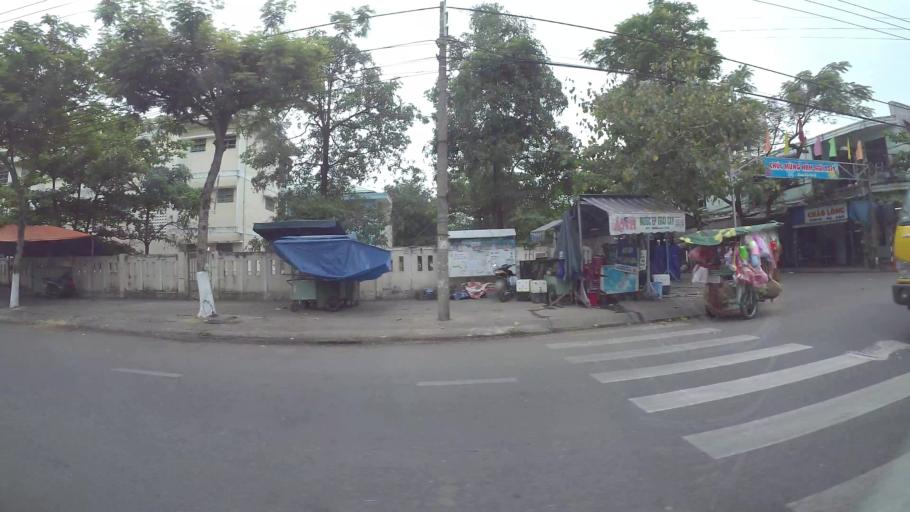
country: VN
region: Da Nang
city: Lien Chieu
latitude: 16.0772
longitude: 108.1657
